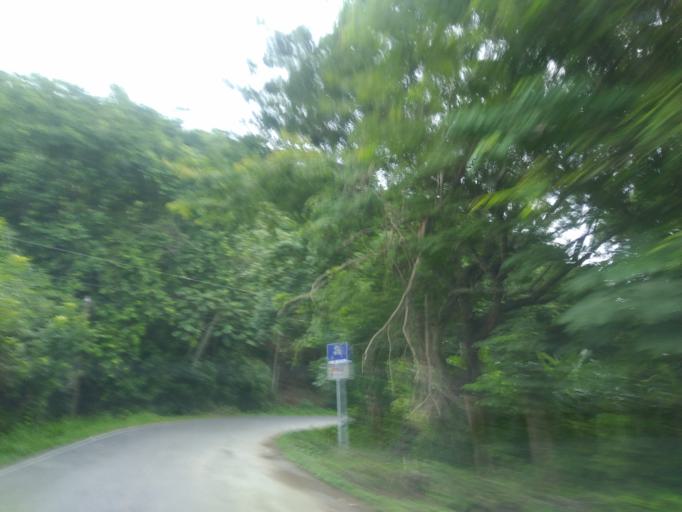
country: CR
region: Puntarenas
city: Paquera
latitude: 9.8227
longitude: -84.9142
